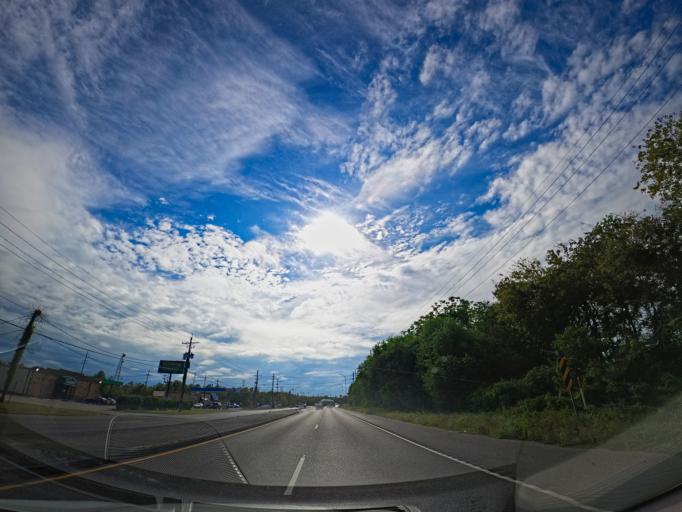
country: US
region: Louisiana
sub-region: Saint Bernard Parish
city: Chalmette
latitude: 30.0421
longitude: -89.8961
